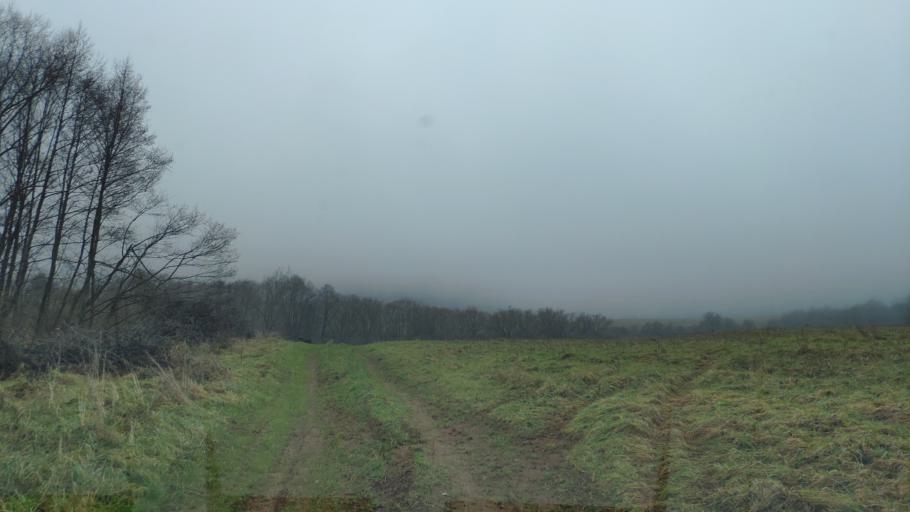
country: SK
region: Banskobystricky
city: Revuca
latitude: 48.6470
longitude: 20.2506
